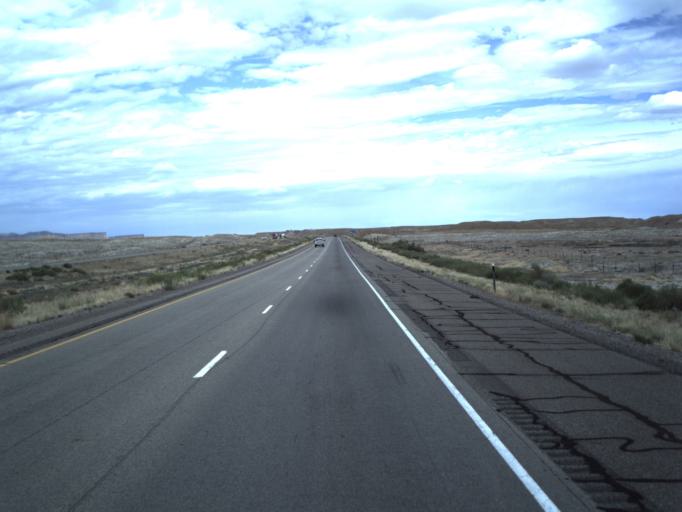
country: US
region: Utah
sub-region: Grand County
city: Moab
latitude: 38.9321
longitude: -109.8626
